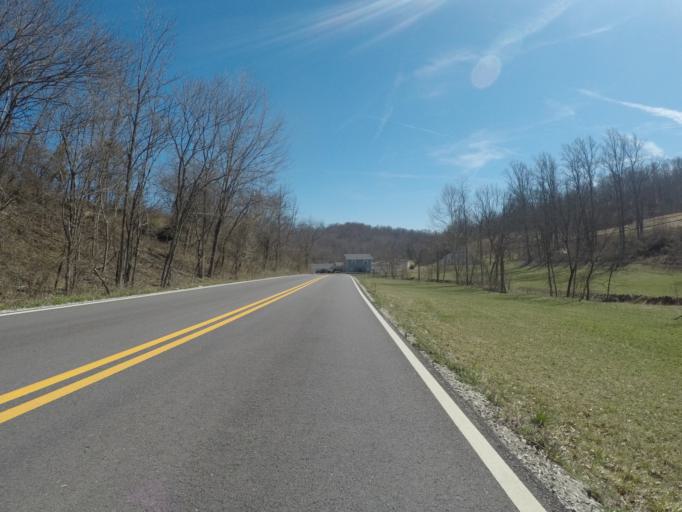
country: US
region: Ohio
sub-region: Lawrence County
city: Burlington
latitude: 38.4553
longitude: -82.5471
